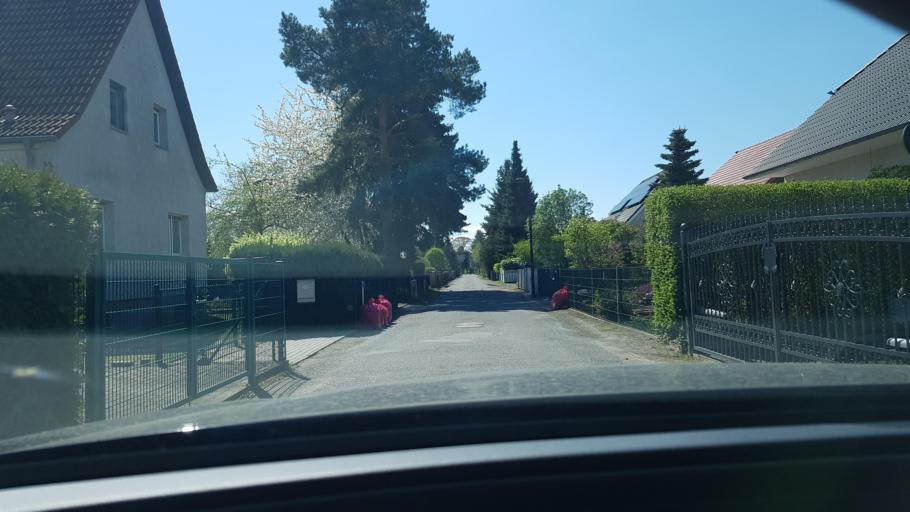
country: DE
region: Brandenburg
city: Rangsdorf
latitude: 52.3402
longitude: 13.4053
